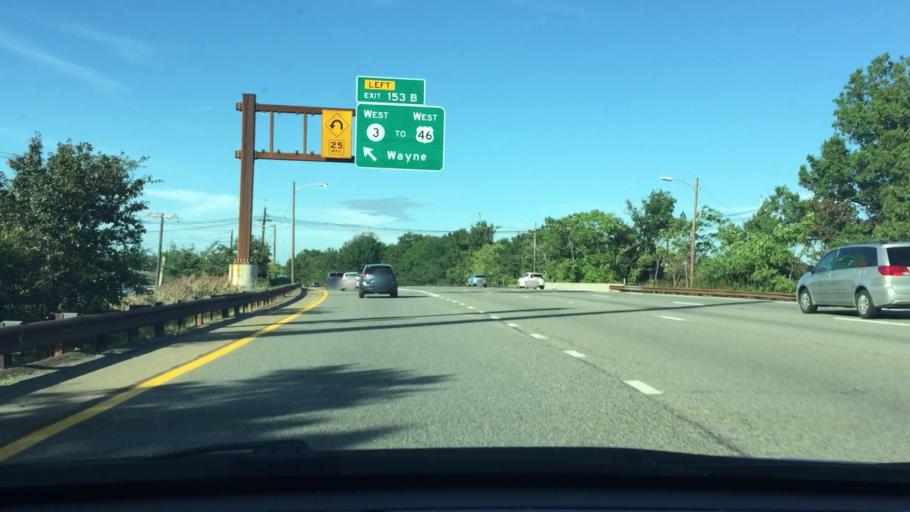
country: US
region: New Jersey
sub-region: Passaic County
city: Clifton
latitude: 40.8529
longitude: -74.1748
